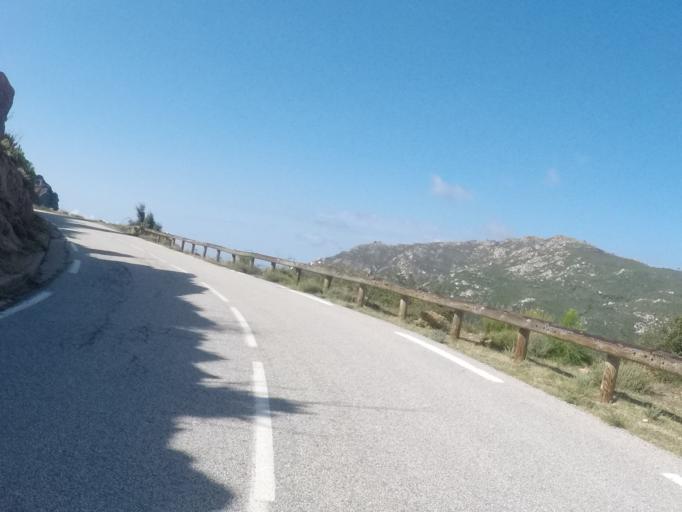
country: FR
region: Corsica
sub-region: Departement de la Corse-du-Sud
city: Olmeto
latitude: 41.7625
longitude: 9.0317
